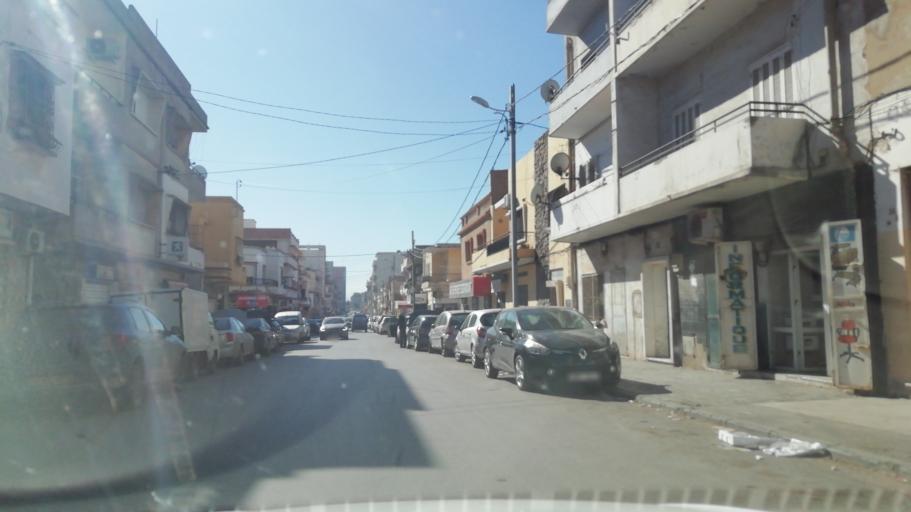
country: DZ
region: Oran
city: Oran
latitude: 35.6964
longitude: -0.6213
